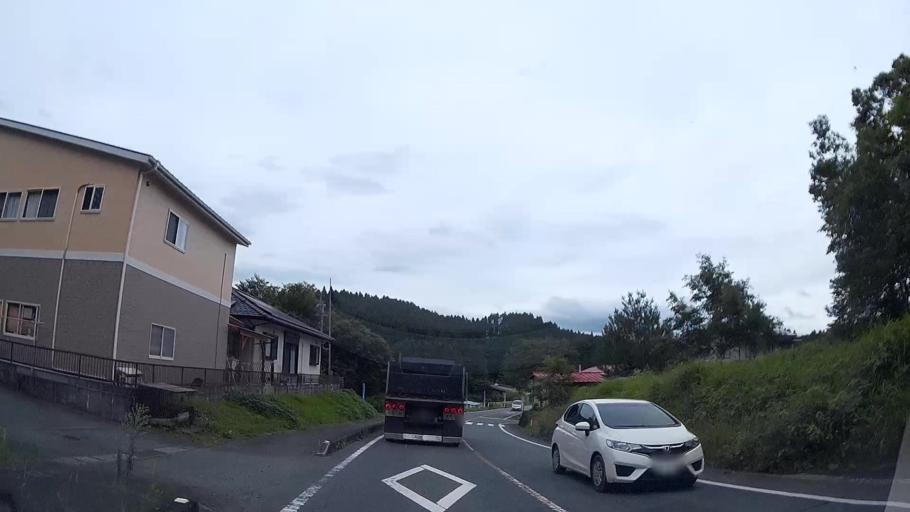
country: JP
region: Oita
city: Tsukawaki
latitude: 33.1239
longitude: 131.0460
